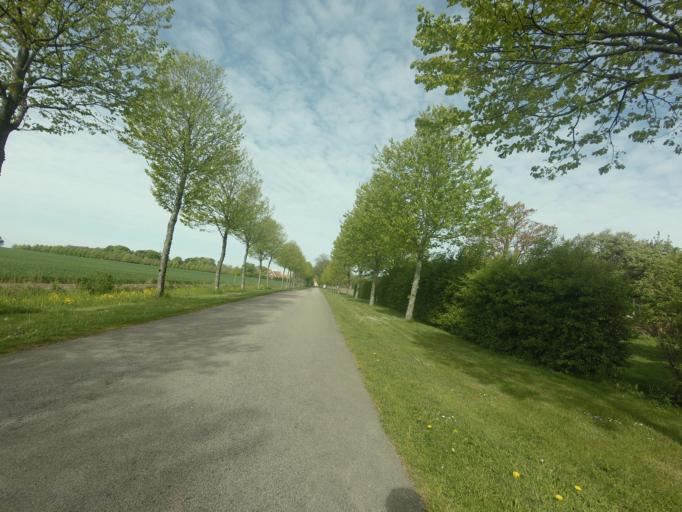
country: SE
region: Skane
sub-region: Hoganas Kommun
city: Hoganas
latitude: 56.2616
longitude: 12.5395
